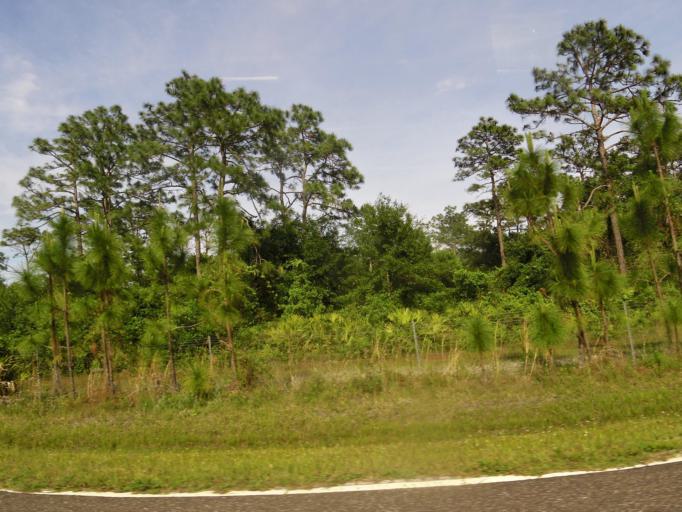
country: US
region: Florida
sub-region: Duval County
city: Atlantic Beach
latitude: 30.4679
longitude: -81.4863
